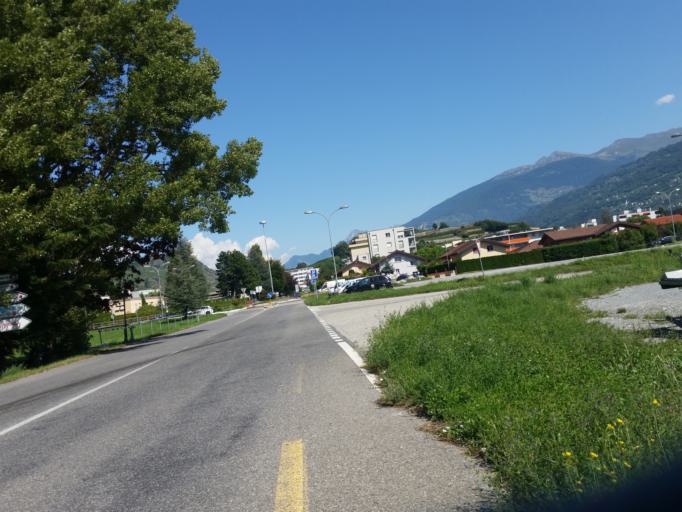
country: CH
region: Valais
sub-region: Conthey District
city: Vetroz
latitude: 46.2179
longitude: 7.2964
